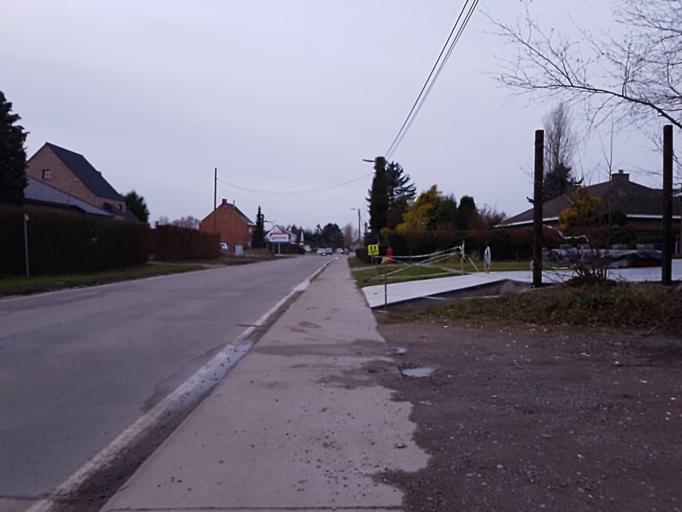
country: BE
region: Flanders
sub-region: Provincie Antwerpen
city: Putte
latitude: 51.0417
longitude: 4.6476
